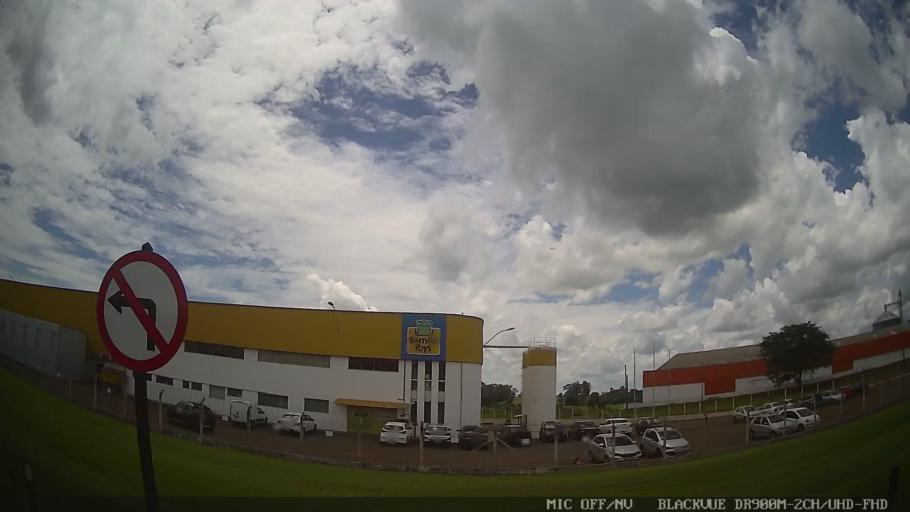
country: BR
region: Sao Paulo
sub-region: Laranjal Paulista
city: Laranjal Paulista
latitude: -23.0417
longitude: -47.9061
